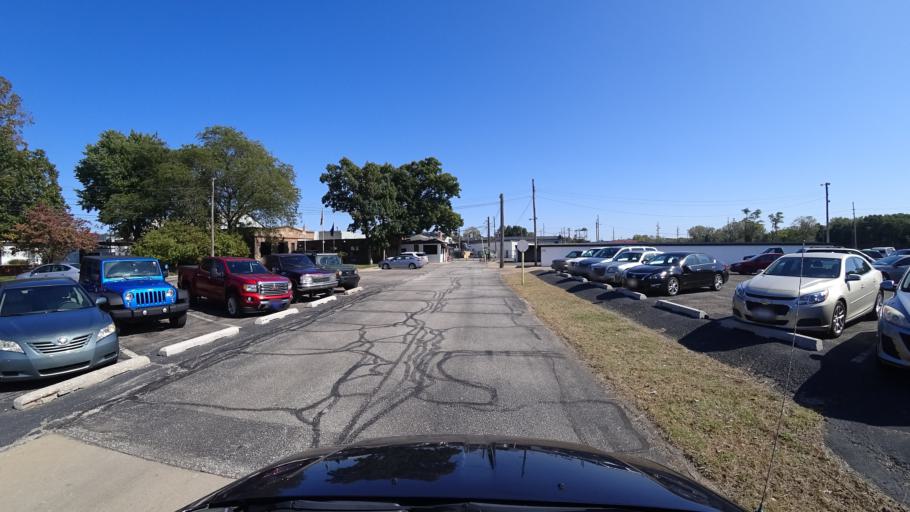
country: US
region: Indiana
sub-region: LaPorte County
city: Michigan City
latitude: 41.7243
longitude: -86.8894
